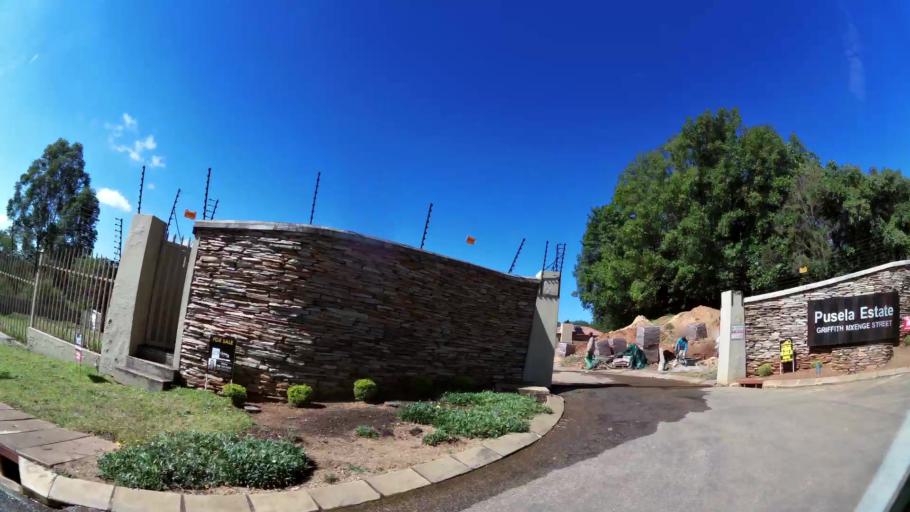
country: ZA
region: Limpopo
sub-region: Mopani District Municipality
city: Tzaneen
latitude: -23.8179
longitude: 30.1561
